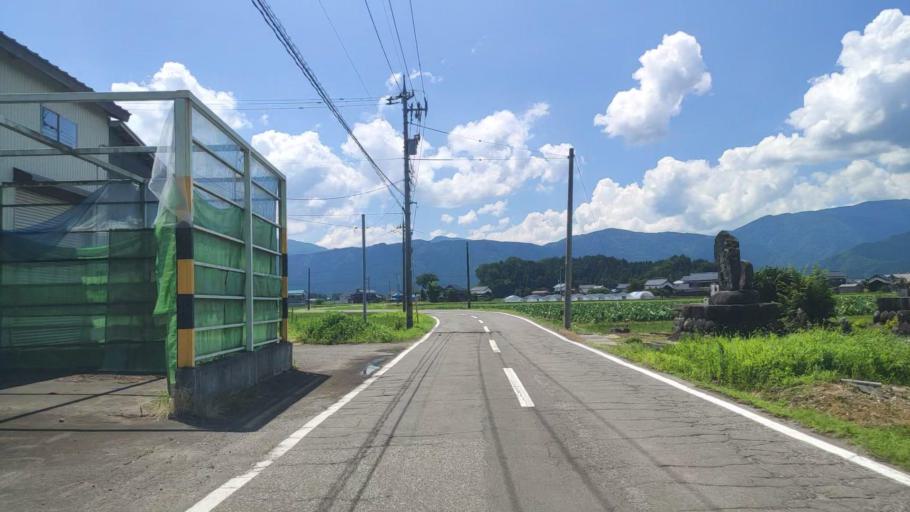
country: JP
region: Fukui
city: Ono
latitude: 35.9733
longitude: 136.5238
